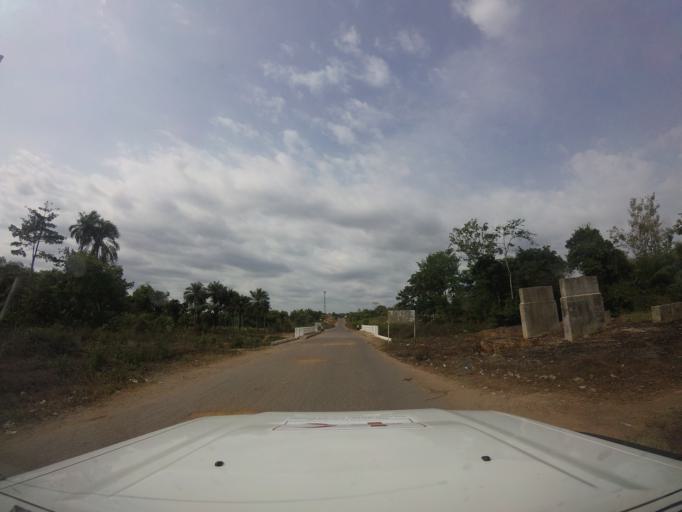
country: LR
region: Bomi
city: Tubmanburg
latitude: 6.6899
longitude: -10.8748
